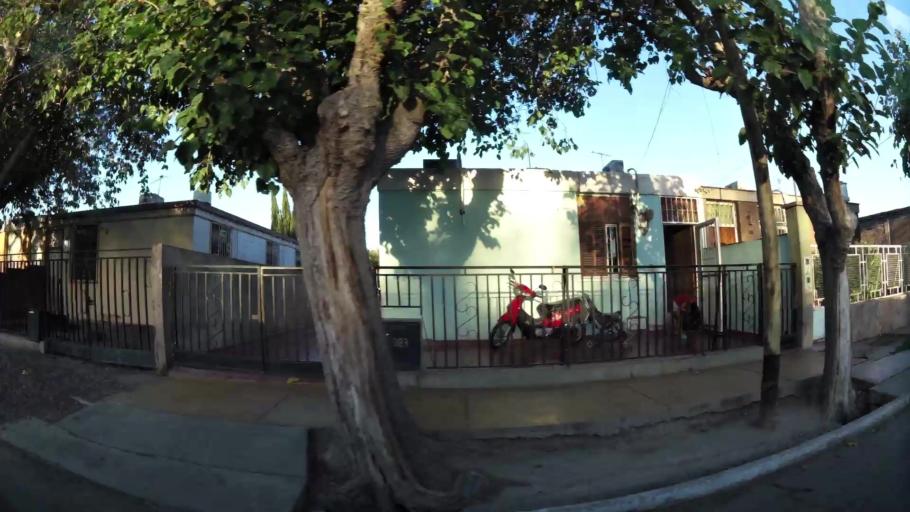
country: AR
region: San Juan
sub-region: Departamento de Santa Lucia
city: Santa Lucia
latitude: -31.5288
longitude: -68.5066
